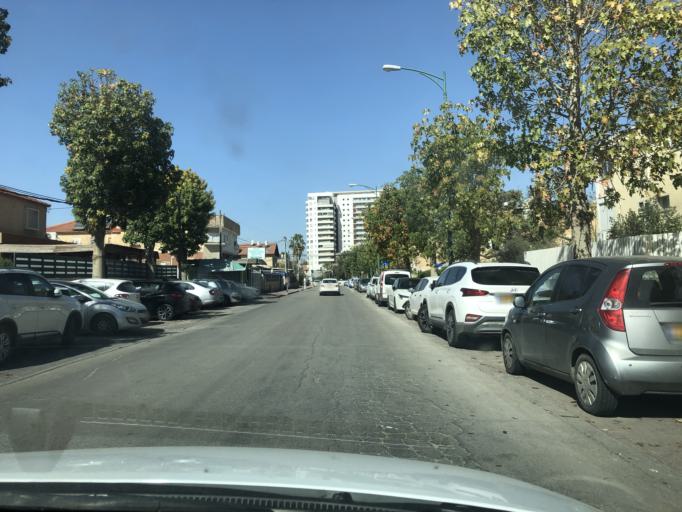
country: IL
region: Southern District
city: Beersheba
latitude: 31.2565
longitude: 34.7952
